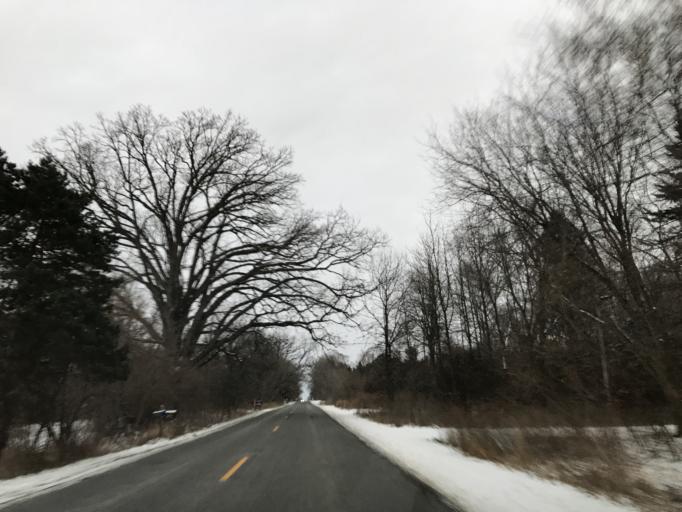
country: US
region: Michigan
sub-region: Washtenaw County
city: Ann Arbor
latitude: 42.3482
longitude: -83.6964
